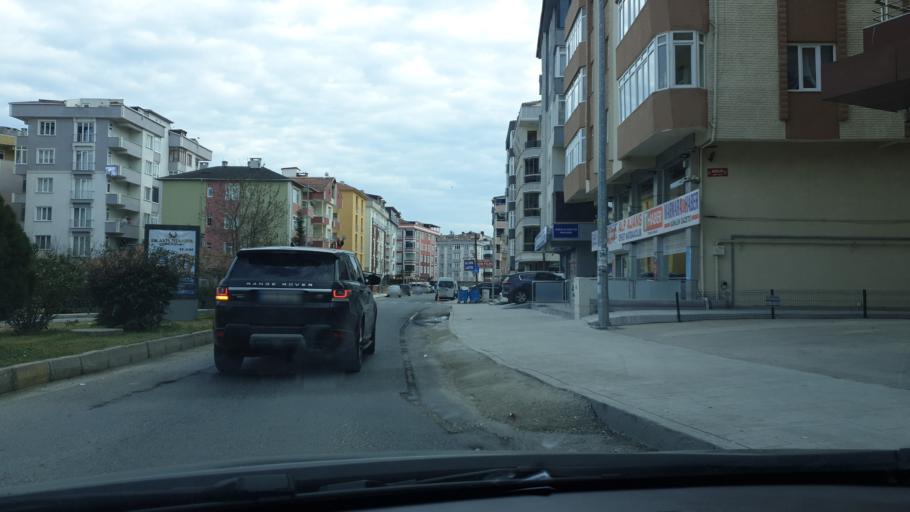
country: TR
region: Tekirdag
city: Cerkezkoey
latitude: 41.2877
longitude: 27.9921
